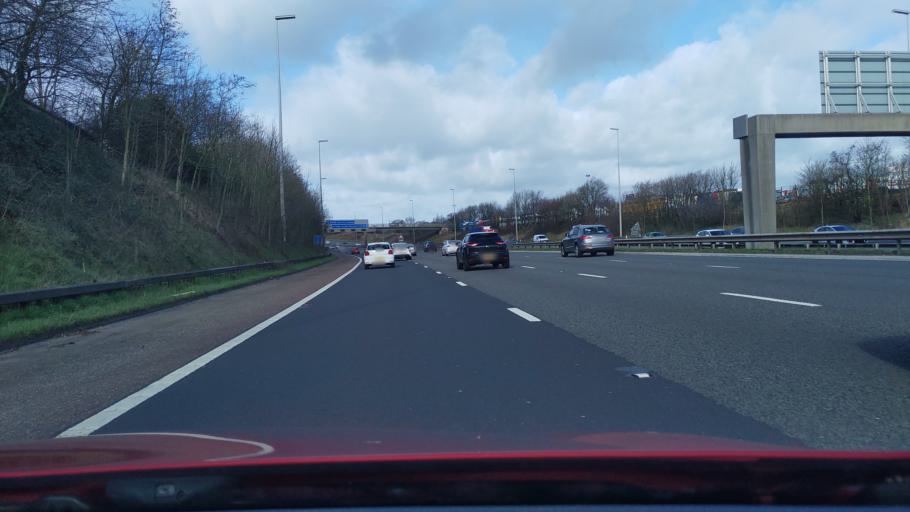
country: GB
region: England
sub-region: Lancashire
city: Goosnargh
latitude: 53.7839
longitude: -2.6512
